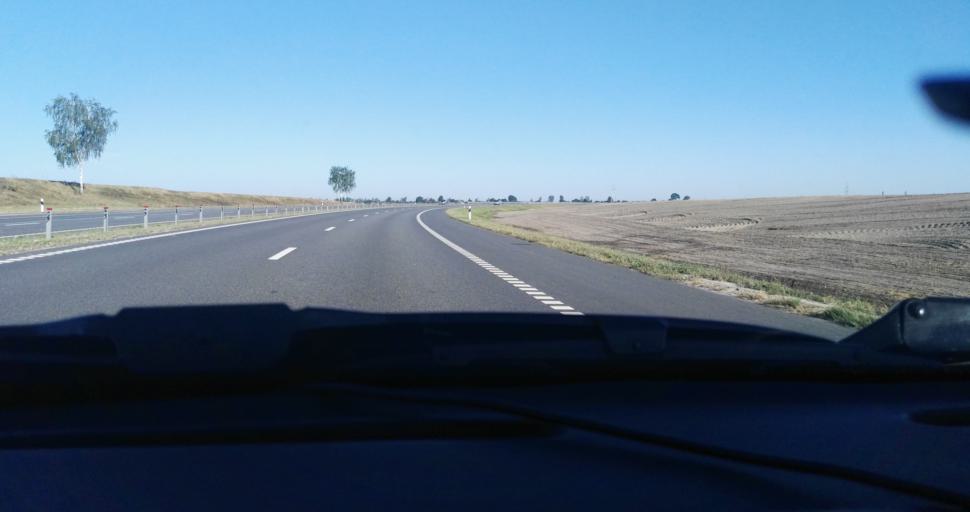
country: BY
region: Gomel
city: Buda-Kashalyova
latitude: 52.5085
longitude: 30.6338
